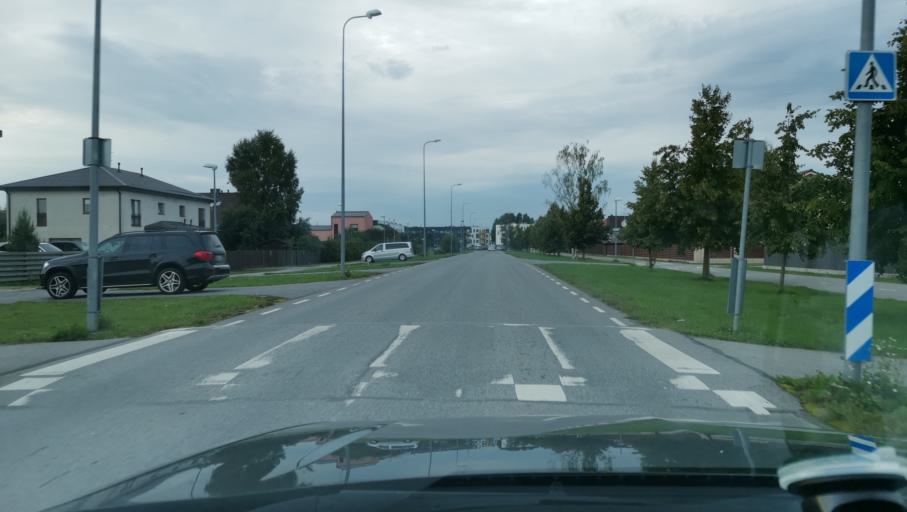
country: EE
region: Harju
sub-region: Saue vald
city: Laagri
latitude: 59.4257
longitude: 24.6217
